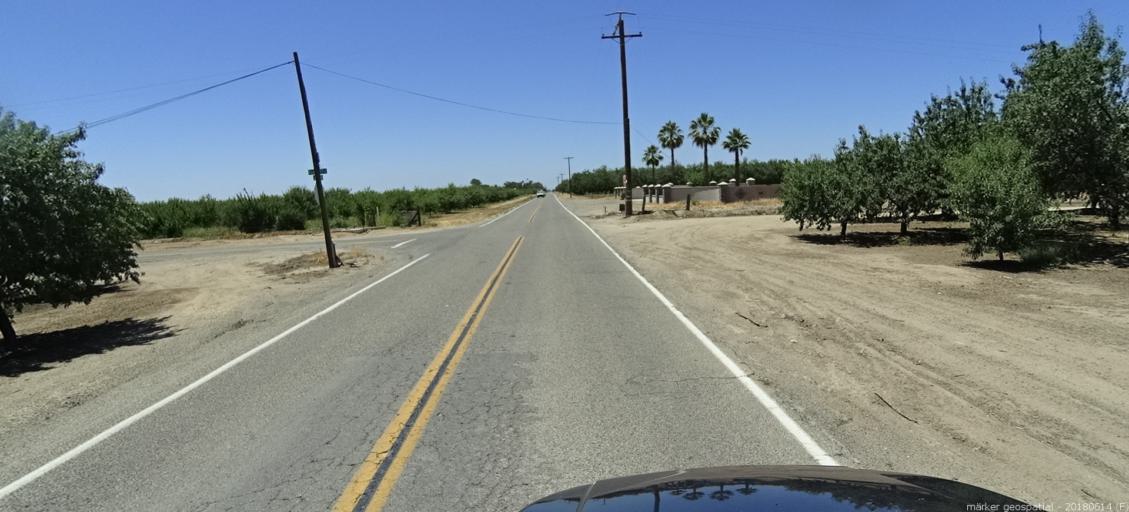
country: US
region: California
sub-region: Madera County
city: Fairmead
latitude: 37.0184
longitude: -120.2293
